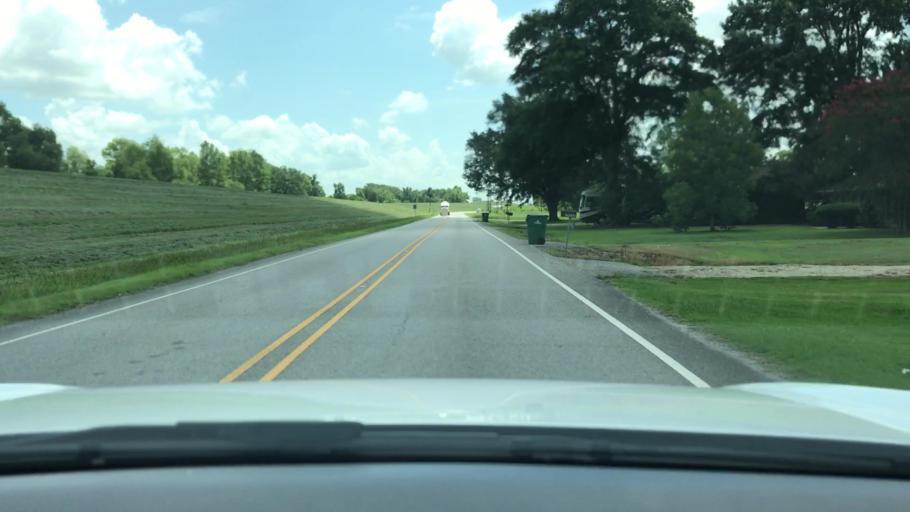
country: US
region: Louisiana
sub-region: Iberville Parish
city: Plaquemine
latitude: 30.2767
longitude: -91.2130
